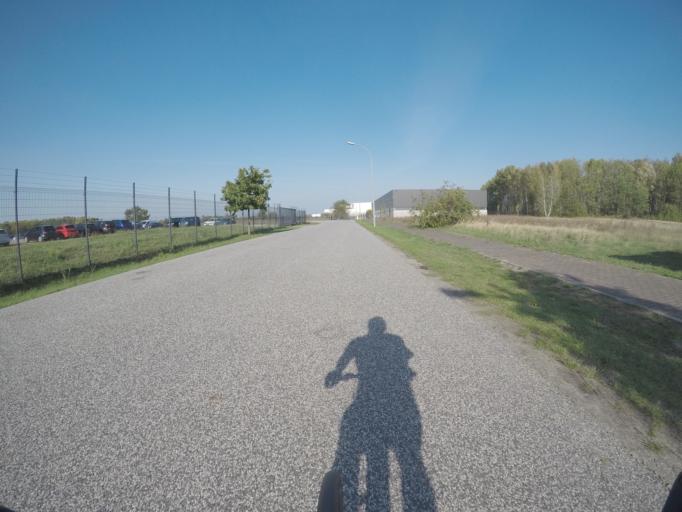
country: DE
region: Brandenburg
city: Leegebruch
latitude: 52.7240
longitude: 13.2203
